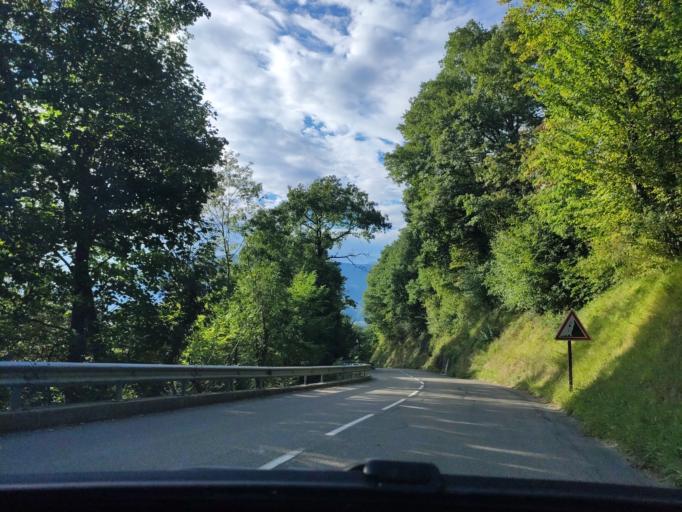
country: FR
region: Rhone-Alpes
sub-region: Departement de l'Isere
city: Gieres
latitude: 45.1760
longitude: 5.7926
